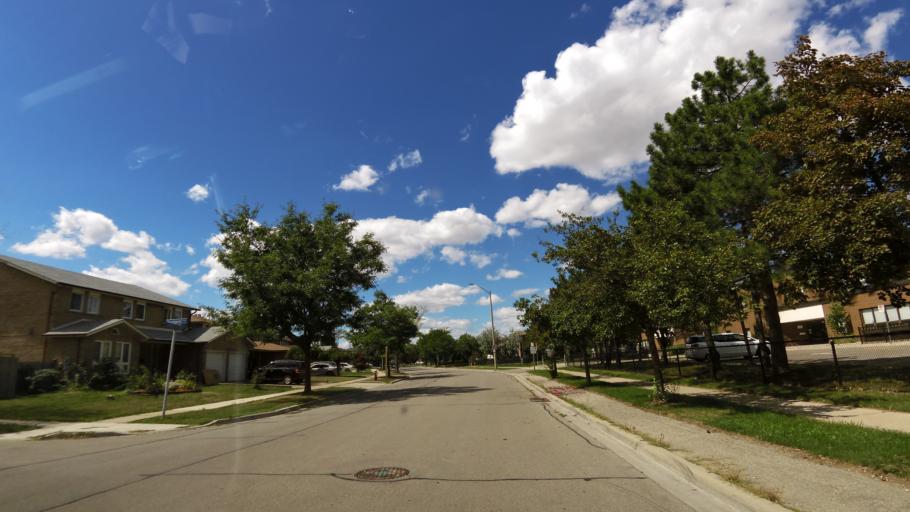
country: CA
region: Ontario
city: Etobicoke
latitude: 43.6228
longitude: -79.6127
